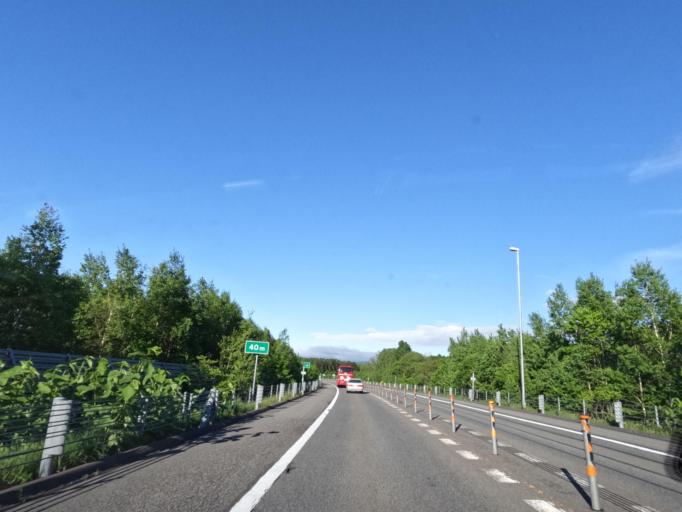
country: JP
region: Hokkaido
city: Kamikawa
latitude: 43.8382
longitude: 142.7248
